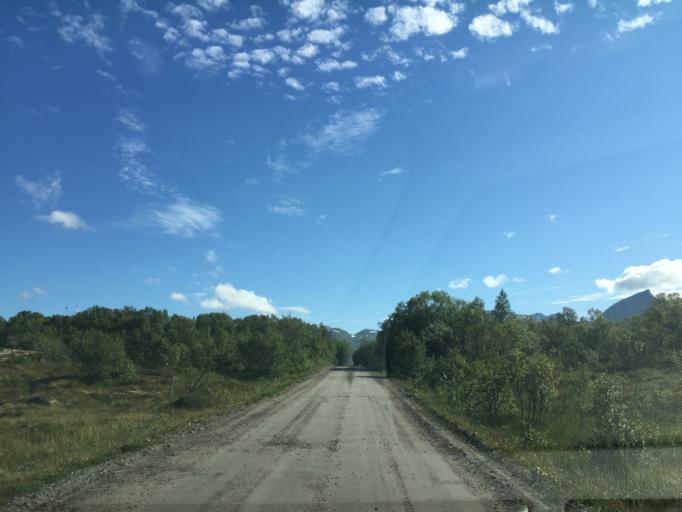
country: NO
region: Nordland
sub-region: Vagan
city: Kabelvag
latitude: 68.3534
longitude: 14.4500
